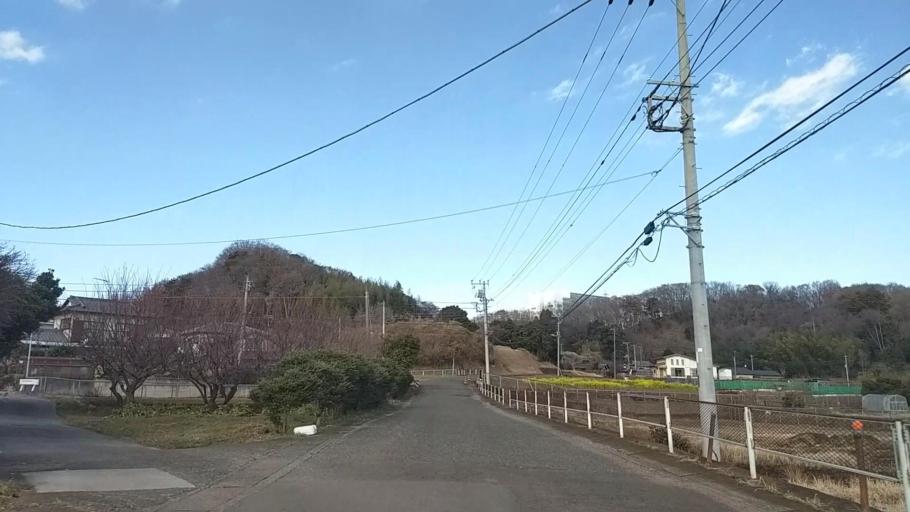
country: JP
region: Kanagawa
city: Isehara
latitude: 35.4156
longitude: 139.3167
